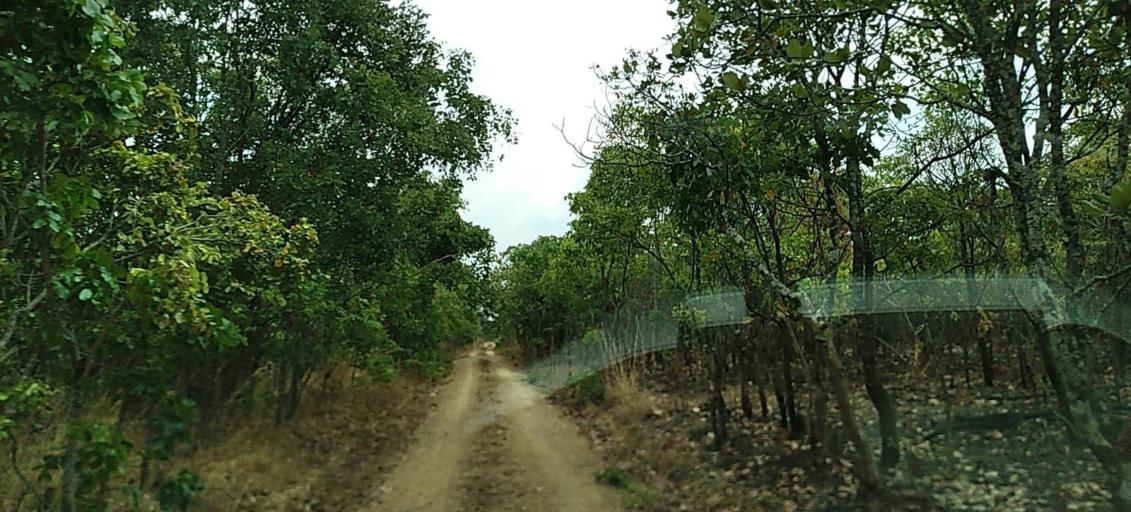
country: ZM
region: Copperbelt
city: Chililabombwe
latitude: -12.3228
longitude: 27.7848
